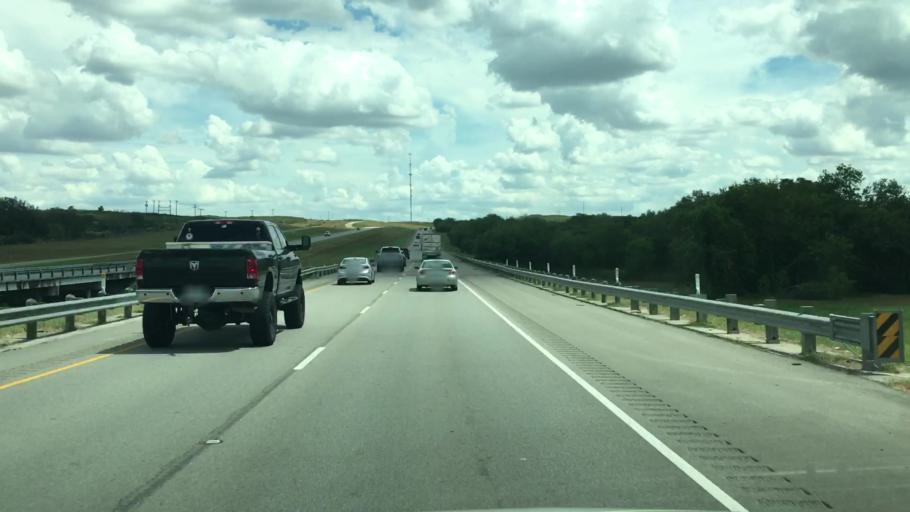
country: US
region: Texas
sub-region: San Patricio County
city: Mathis
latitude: 28.2621
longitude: -97.9313
